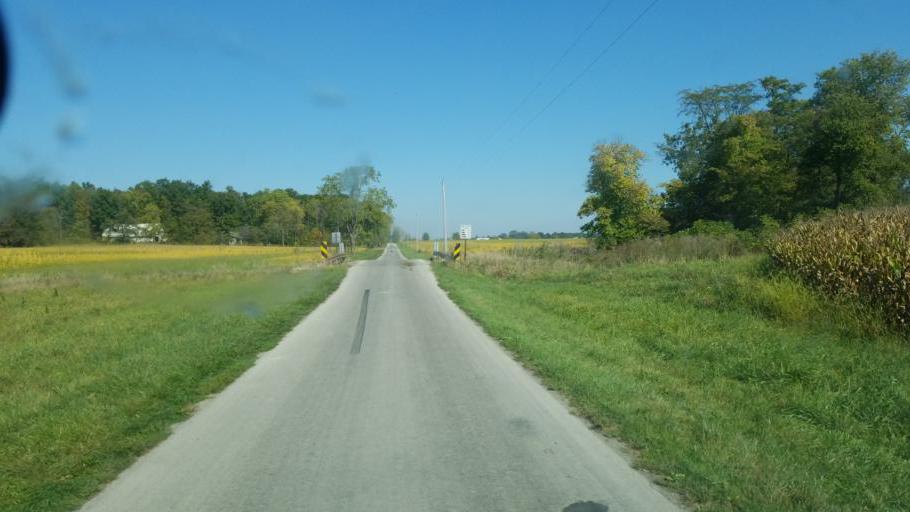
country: US
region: Ohio
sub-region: Hardin County
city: Kenton
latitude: 40.5540
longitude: -83.4854
